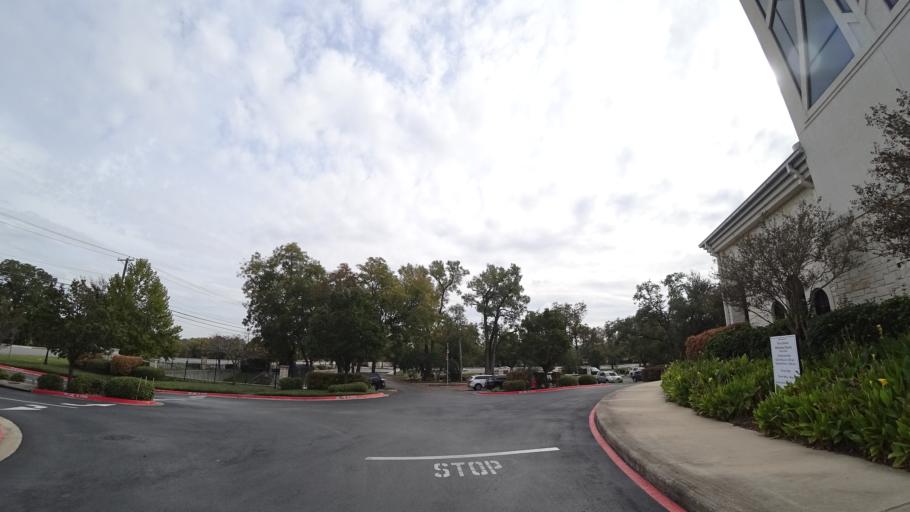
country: US
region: Texas
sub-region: Williamson County
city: Round Rock
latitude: 30.5164
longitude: -97.6828
